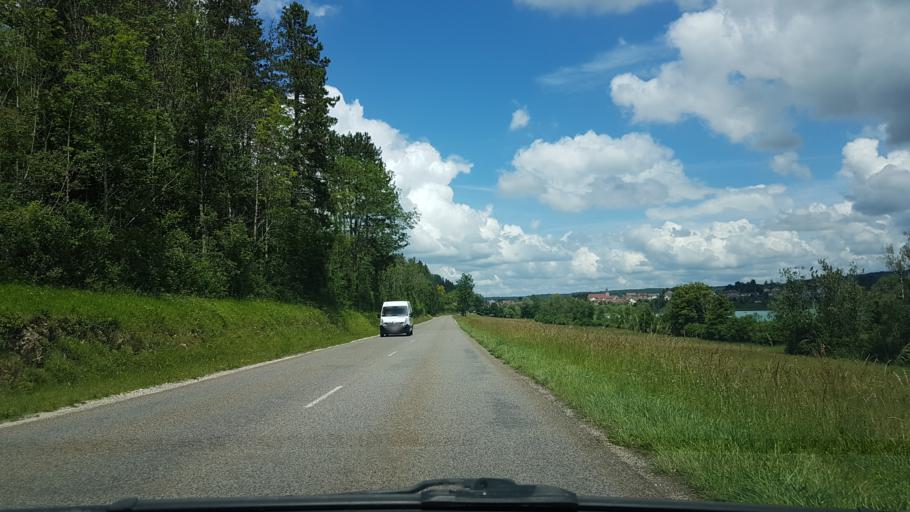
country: FR
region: Franche-Comte
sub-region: Departement du Jura
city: Clairvaux-les-Lacs
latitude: 46.5640
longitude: 5.7440
